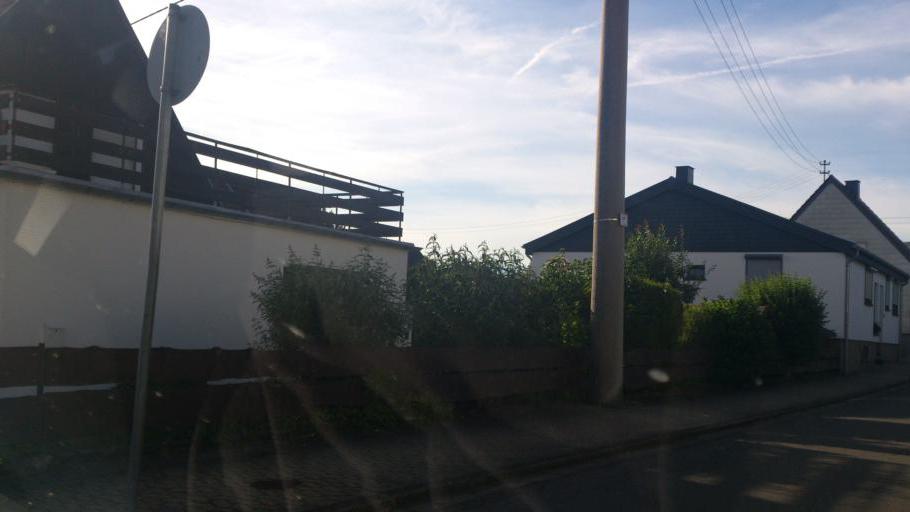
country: DE
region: Saarland
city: Bexbach
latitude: 49.3529
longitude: 7.2622
